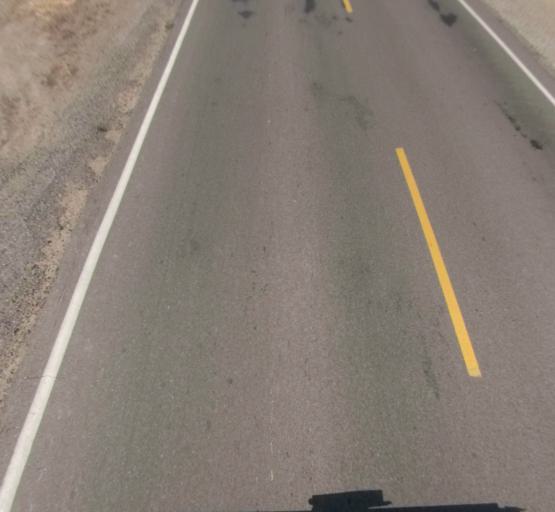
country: US
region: California
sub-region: Madera County
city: Fairmead
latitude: 37.0241
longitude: -120.2569
